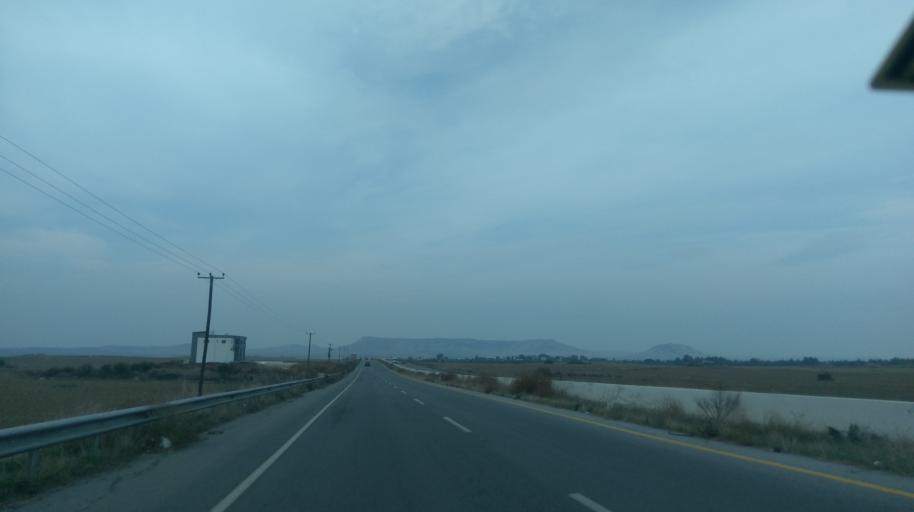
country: CY
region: Lefkosia
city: Mammari
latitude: 35.2126
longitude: 33.2013
